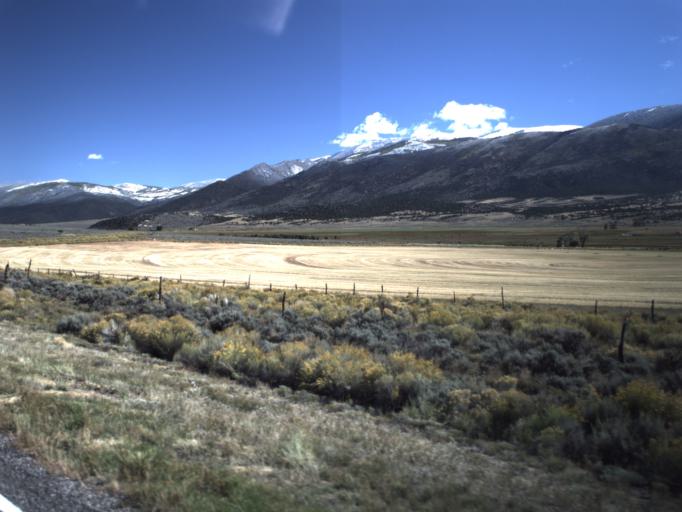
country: US
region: Utah
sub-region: Sevier County
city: Monroe
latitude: 38.5281
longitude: -111.8797
